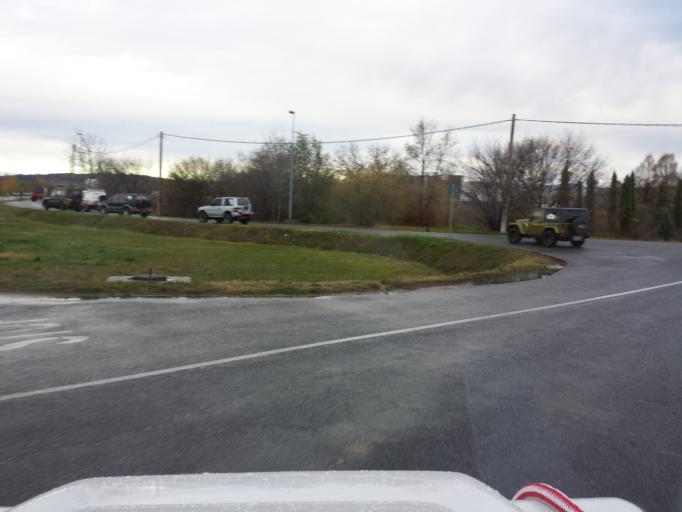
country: IT
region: Friuli Venezia Giulia
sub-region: Provincia di Gorizia
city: Mariano del Friuli
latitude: 45.9003
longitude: 13.4713
